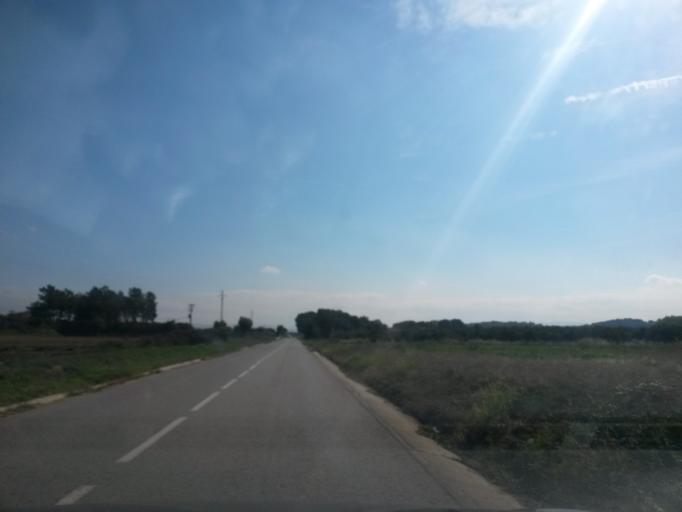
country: ES
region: Catalonia
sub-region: Provincia de Girona
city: Bescano
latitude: 41.9405
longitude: 2.7305
